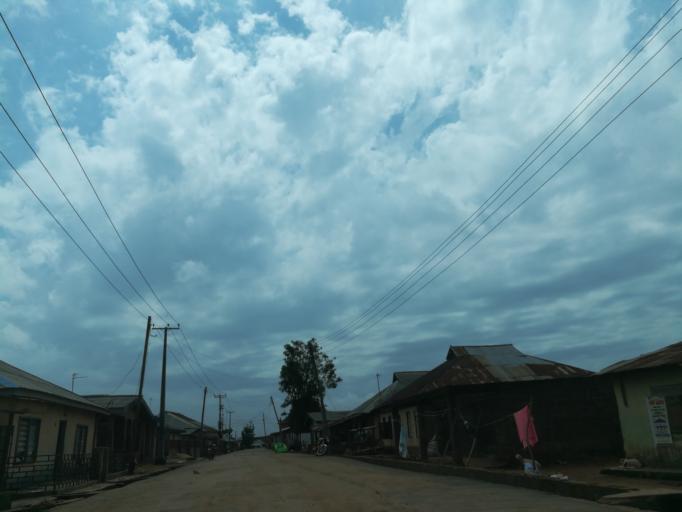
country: NG
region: Lagos
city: Ejirin
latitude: 6.6430
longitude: 3.7116
